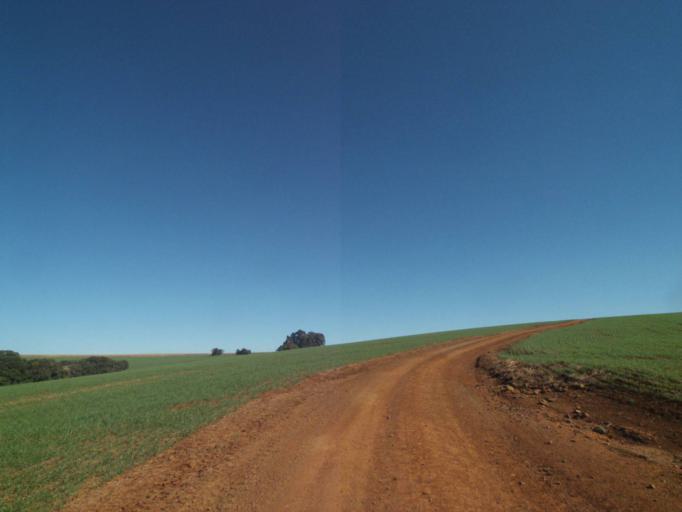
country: BR
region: Parana
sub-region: Tibagi
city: Tibagi
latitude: -24.3891
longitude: -50.3272
